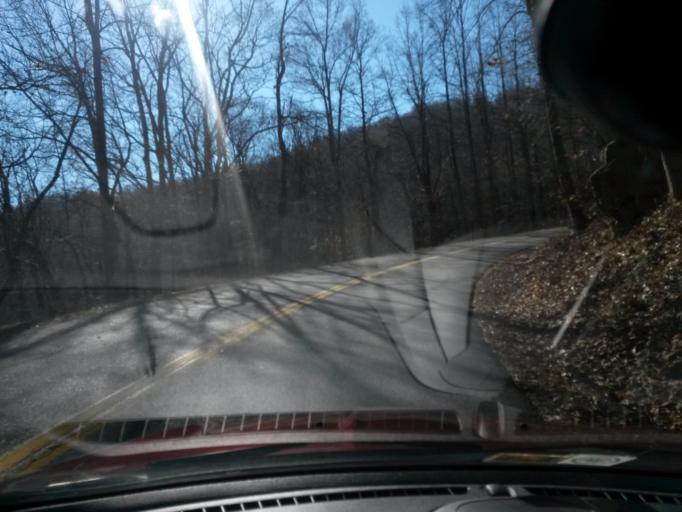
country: US
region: Virginia
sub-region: Botetourt County
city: Buchanan
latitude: 37.4645
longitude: -79.6341
